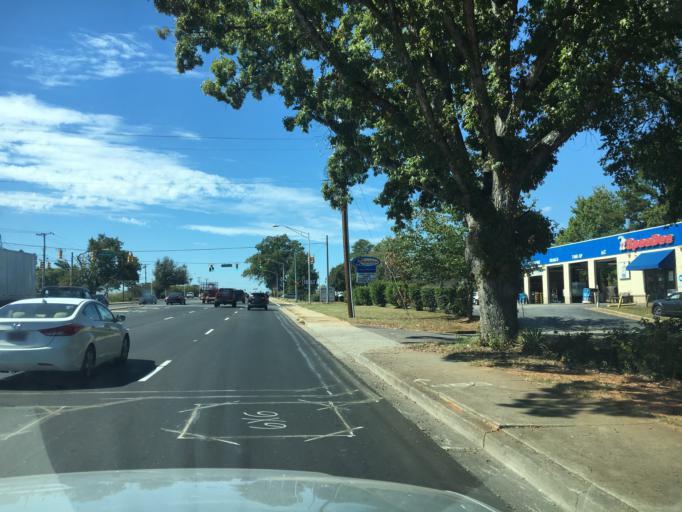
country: US
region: South Carolina
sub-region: Spartanburg County
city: Arcadia
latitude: 34.9374
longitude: -81.9822
